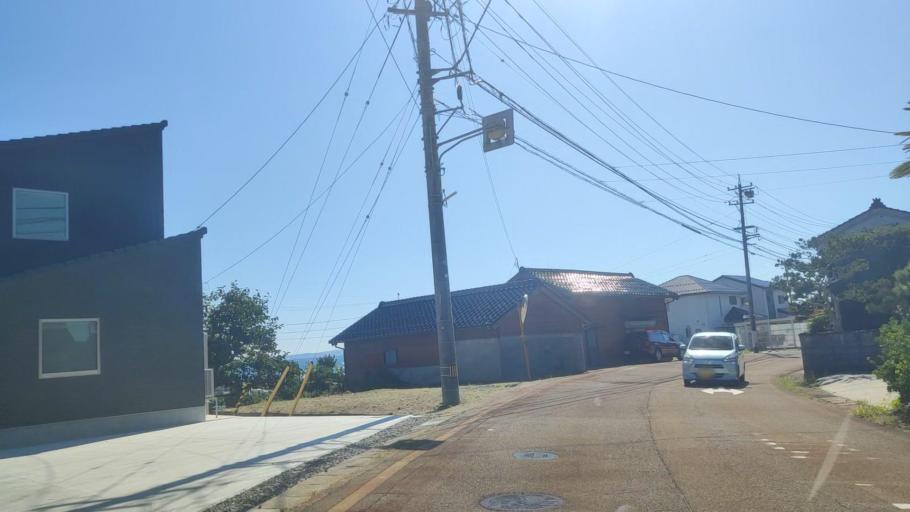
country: JP
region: Ishikawa
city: Nanao
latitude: 37.4408
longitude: 137.2751
